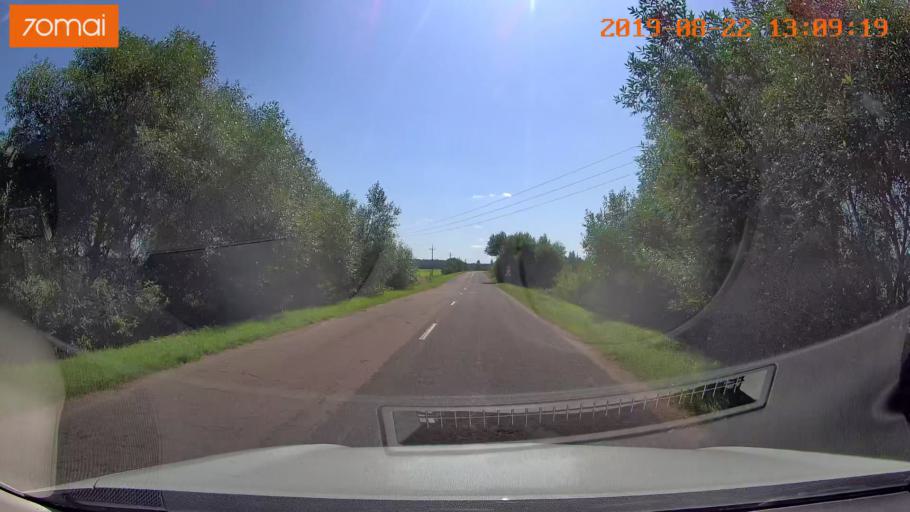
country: BY
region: Minsk
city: Prawdzinski
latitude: 53.3116
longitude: 27.8506
